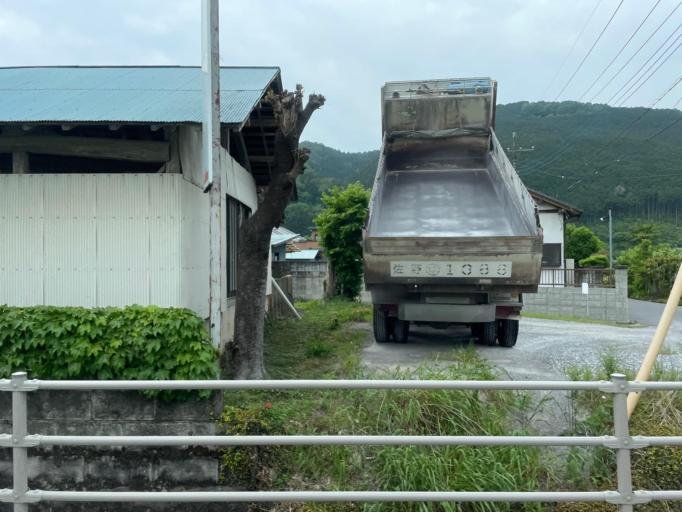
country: JP
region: Tochigi
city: Tochigi
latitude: 36.4393
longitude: 139.6556
